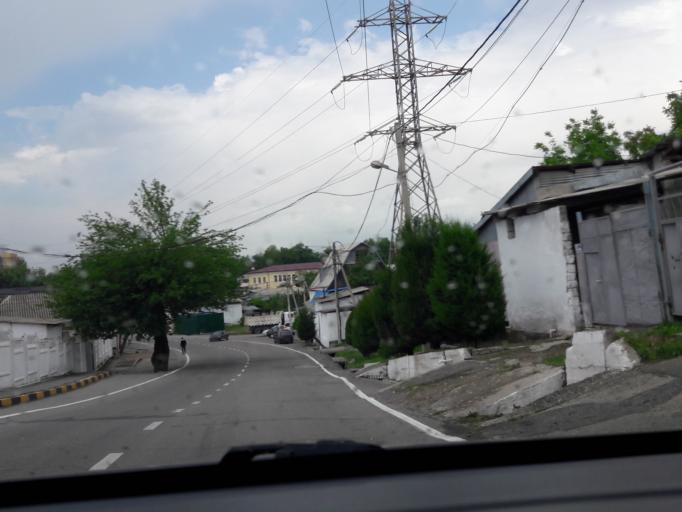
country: TJ
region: Dushanbe
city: Dushanbe
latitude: 38.5802
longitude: 68.8045
